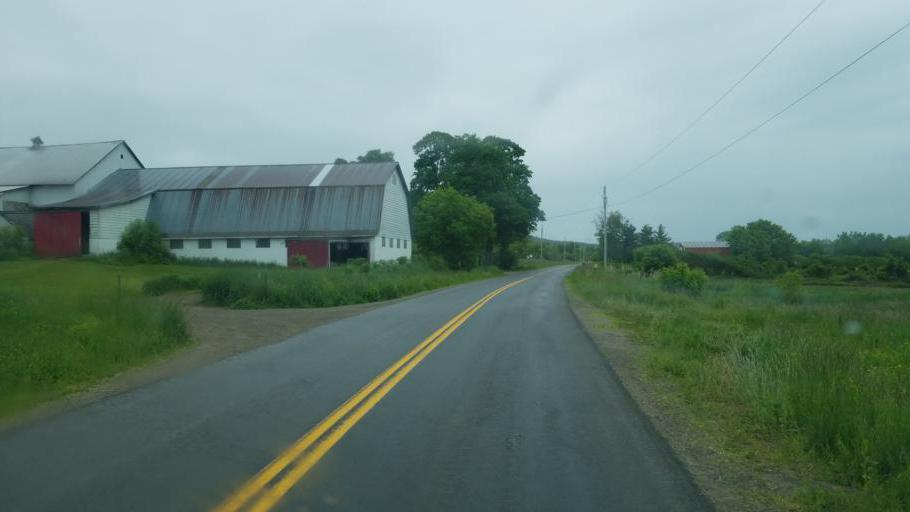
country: US
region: New York
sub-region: Herkimer County
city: Frankfort
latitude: 43.0945
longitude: -75.0984
